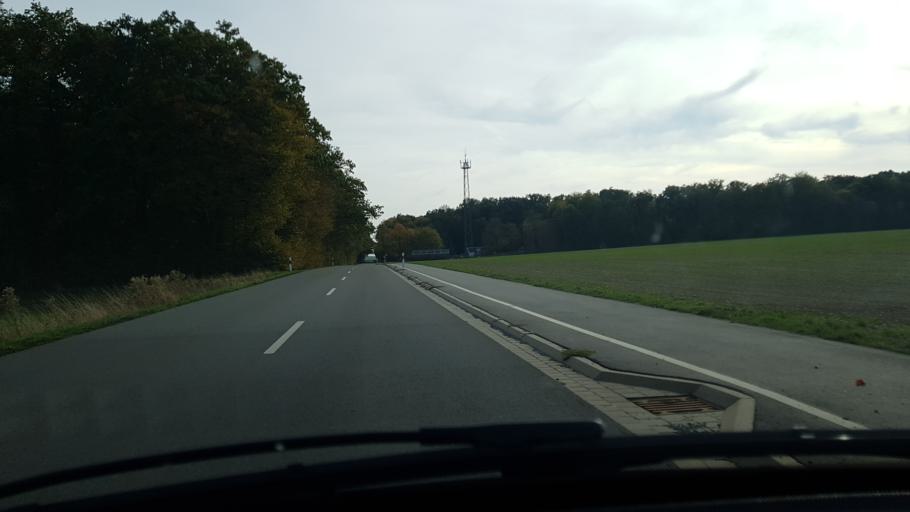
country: DE
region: Lower Saxony
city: Lehre
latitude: 52.3687
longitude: 10.6726
